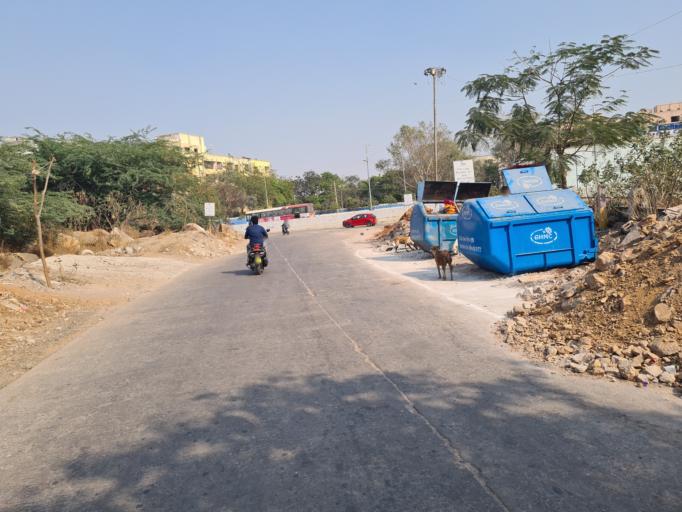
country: IN
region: Telangana
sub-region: Medak
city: Serilingampalle
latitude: 17.4857
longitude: 78.3120
